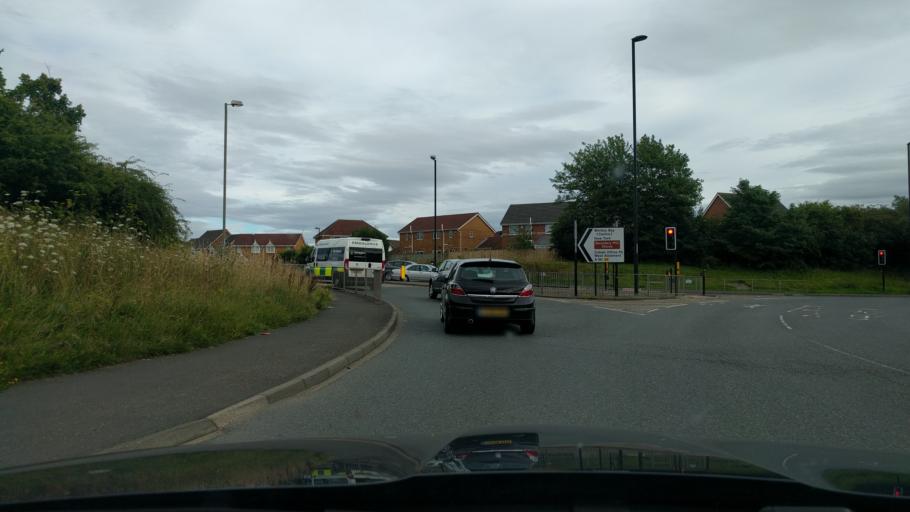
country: GB
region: England
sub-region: Borough of North Tyneside
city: Shiremoor
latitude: 55.0291
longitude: -1.5217
